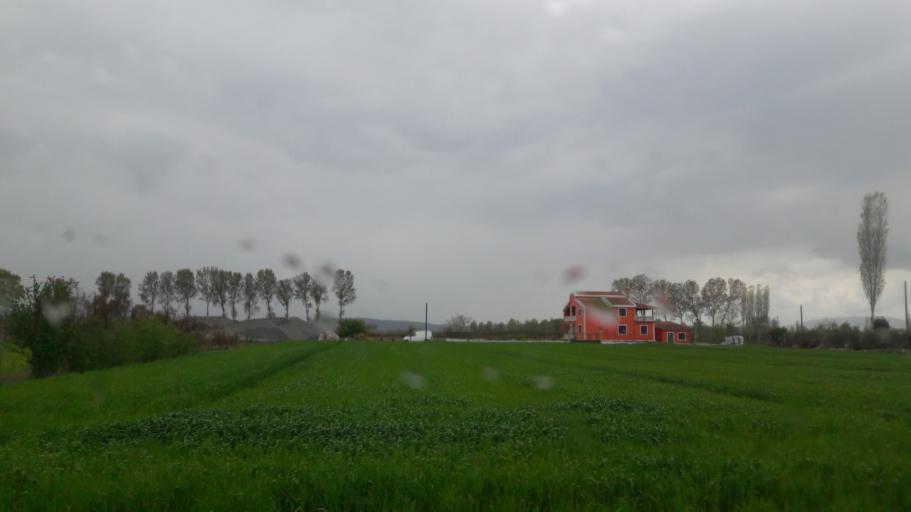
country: AL
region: Shkoder
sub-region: Rrethi i Shkodres
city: Berdica e Madhe
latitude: 41.9696
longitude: 19.4972
